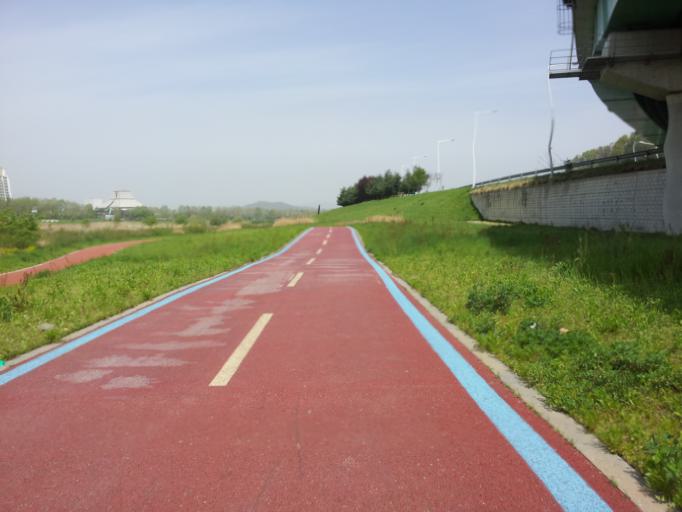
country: KR
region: Daejeon
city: Daejeon
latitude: 36.3625
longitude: 127.4000
